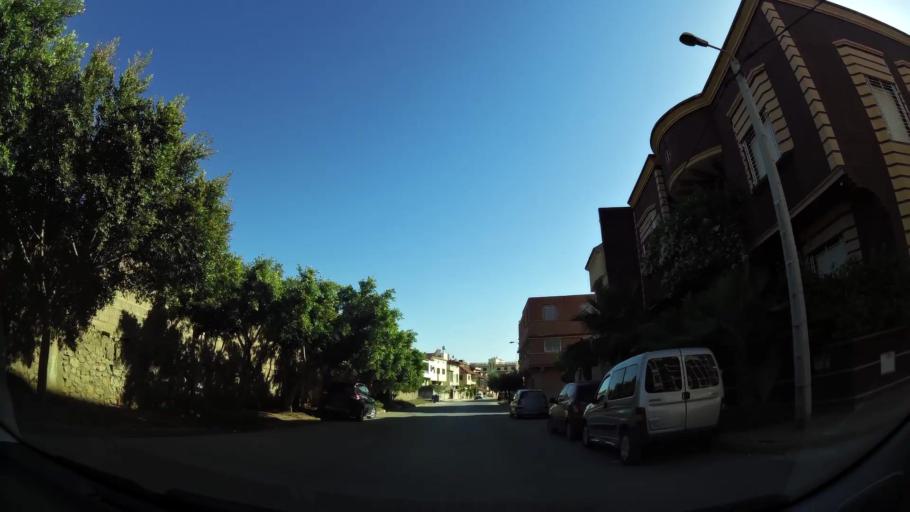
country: MA
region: Oriental
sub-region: Berkane-Taourirt
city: Berkane
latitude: 34.9328
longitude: -2.3281
